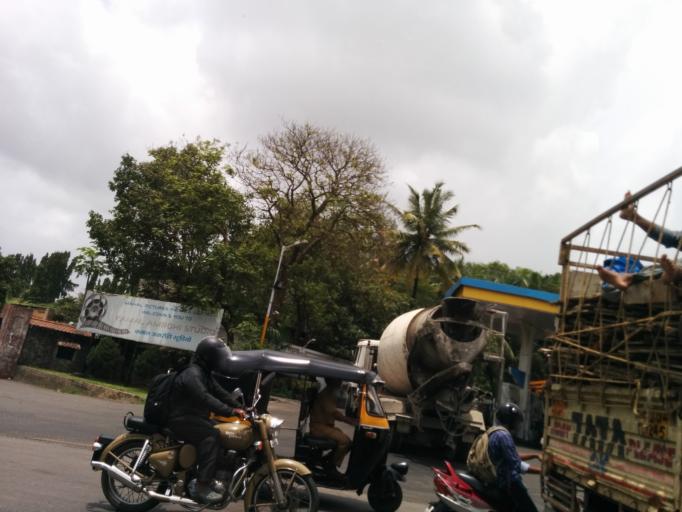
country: IN
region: Maharashtra
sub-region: Mumbai Suburban
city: Powai
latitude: 19.1348
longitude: 72.8743
